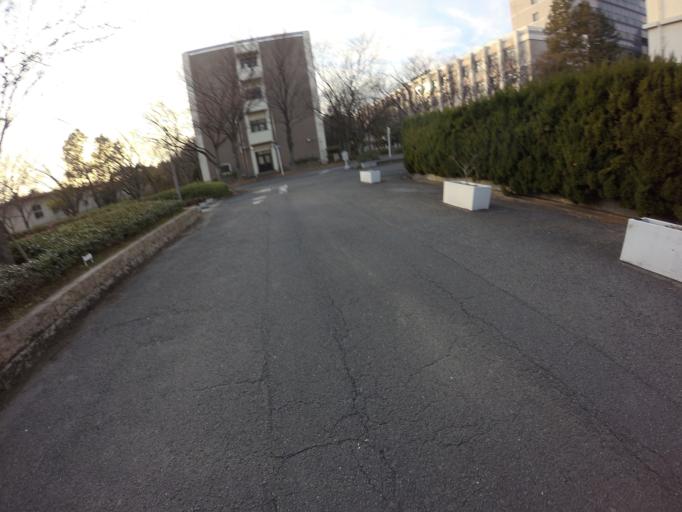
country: JP
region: Osaka
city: Sakai
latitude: 34.5903
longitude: 135.5047
